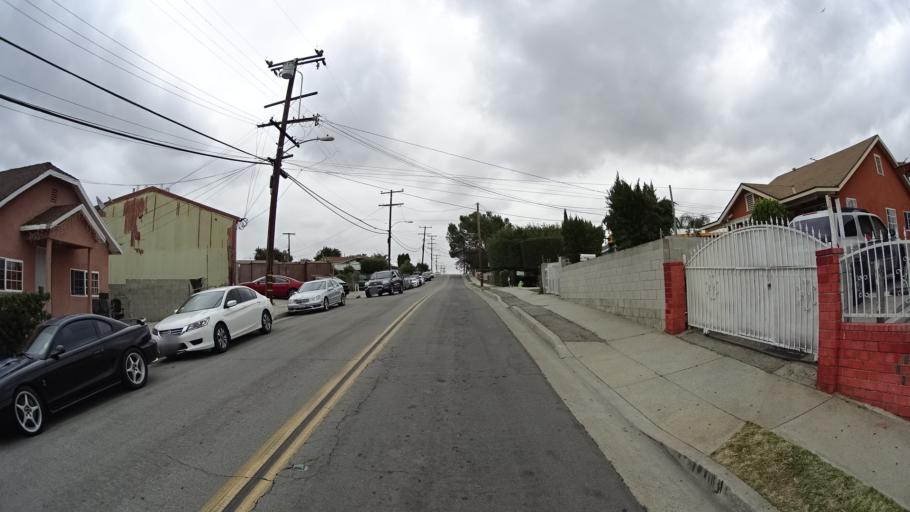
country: US
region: California
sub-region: Los Angeles County
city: Boyle Heights
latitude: 34.0565
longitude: -118.1915
